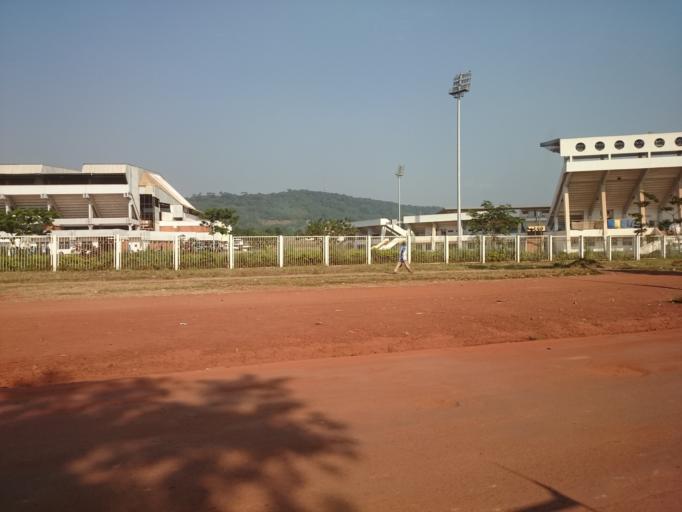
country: CF
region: Bangui
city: Bangui
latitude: 4.3753
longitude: 18.5625
